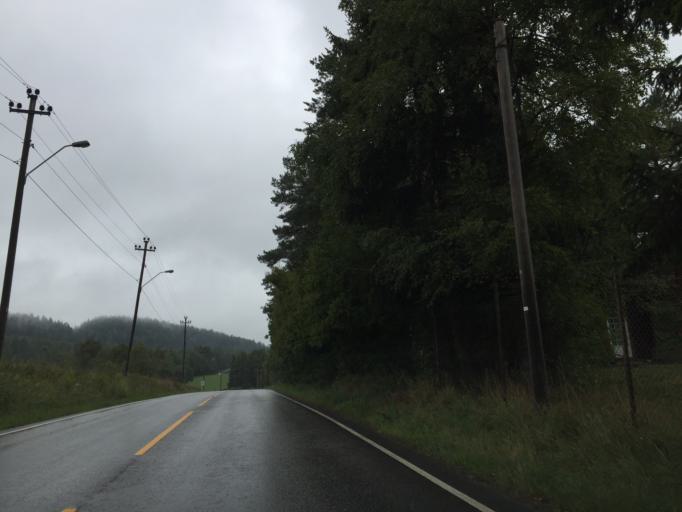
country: NO
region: Akershus
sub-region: Baerum
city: Lysaker
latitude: 59.9860
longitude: 10.6215
